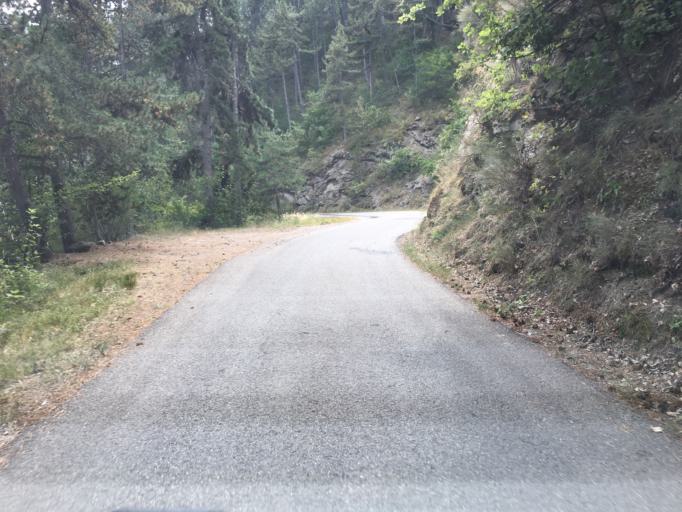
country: FR
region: Provence-Alpes-Cote d'Azur
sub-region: Departement des Alpes-de-Haute-Provence
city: Digne-les-Bains
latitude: 44.2082
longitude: 6.1503
